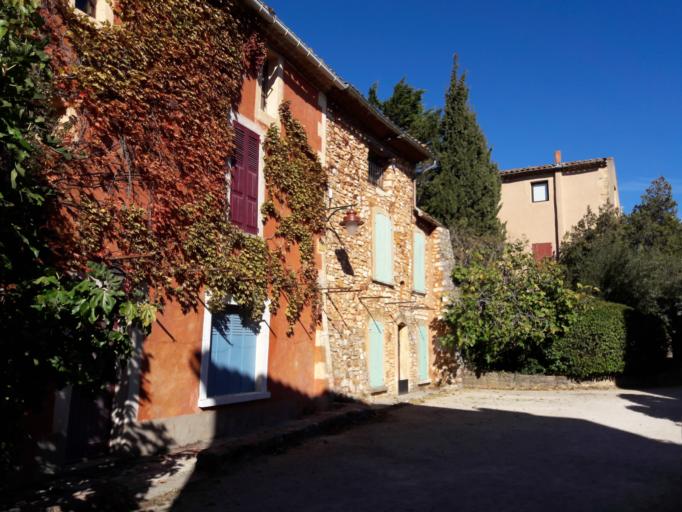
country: FR
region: Provence-Alpes-Cote d'Azur
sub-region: Departement du Vaucluse
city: Roussillon
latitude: 43.9029
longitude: 5.2918
